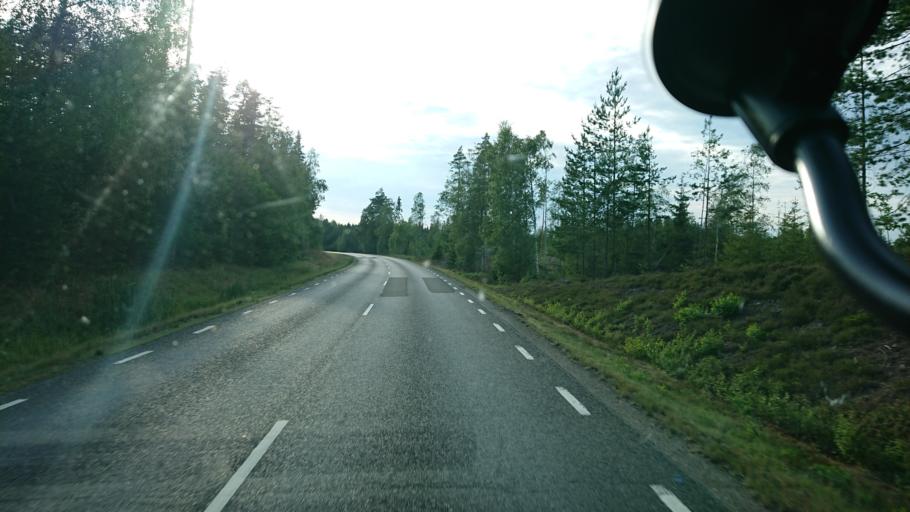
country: SE
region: Kronoberg
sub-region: Vaxjo Kommun
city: Braas
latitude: 57.0240
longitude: 15.0055
